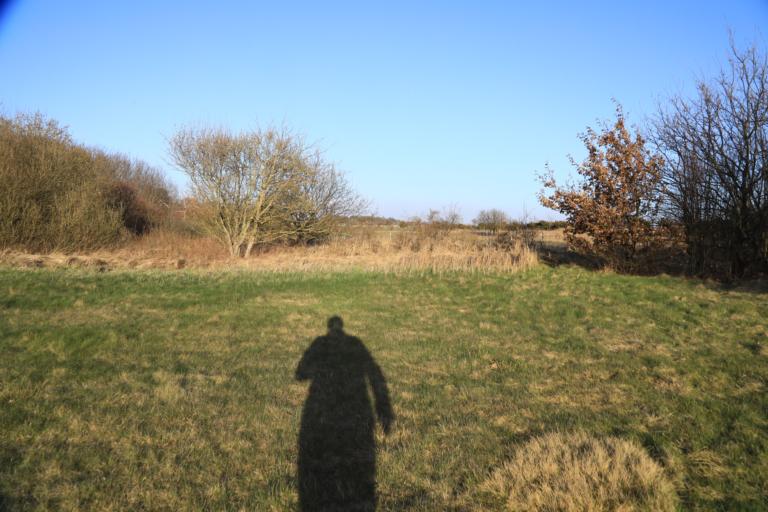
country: SE
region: Halland
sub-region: Varbergs Kommun
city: Varberg
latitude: 57.0895
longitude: 12.2467
